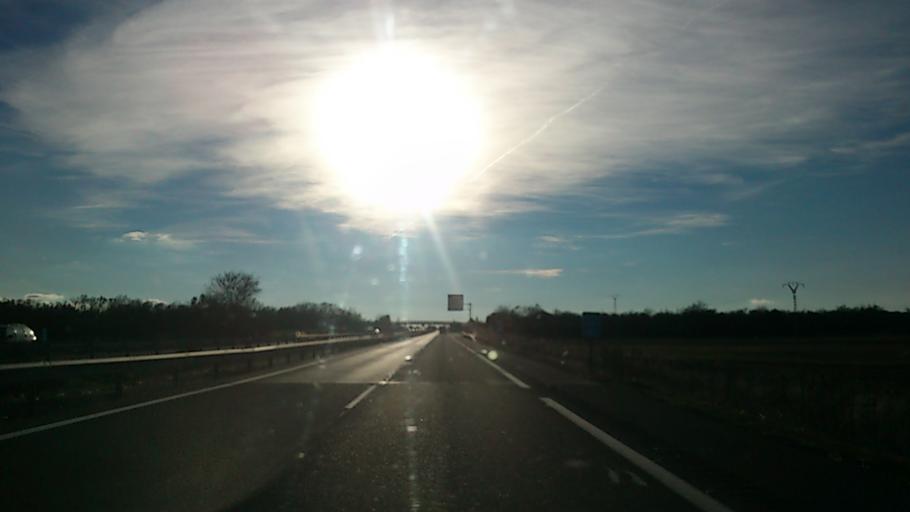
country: ES
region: Castille-La Mancha
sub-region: Provincia de Guadalajara
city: Mirabueno
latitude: 40.9167
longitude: -2.7325
